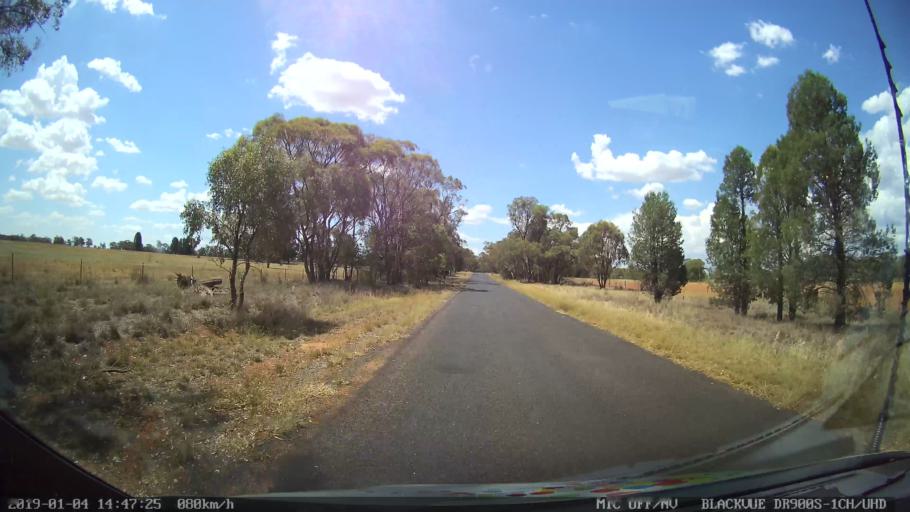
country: AU
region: New South Wales
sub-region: Dubbo Municipality
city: Dubbo
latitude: -32.0694
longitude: 148.6602
